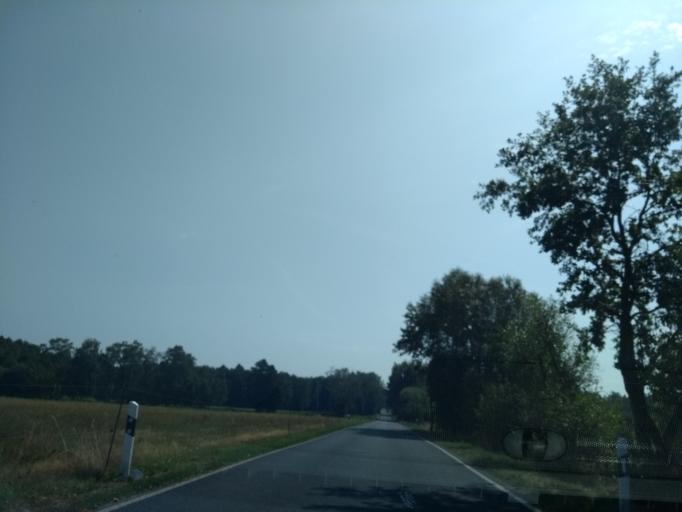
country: DE
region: Brandenburg
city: Vetschau
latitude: 51.8144
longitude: 14.0469
